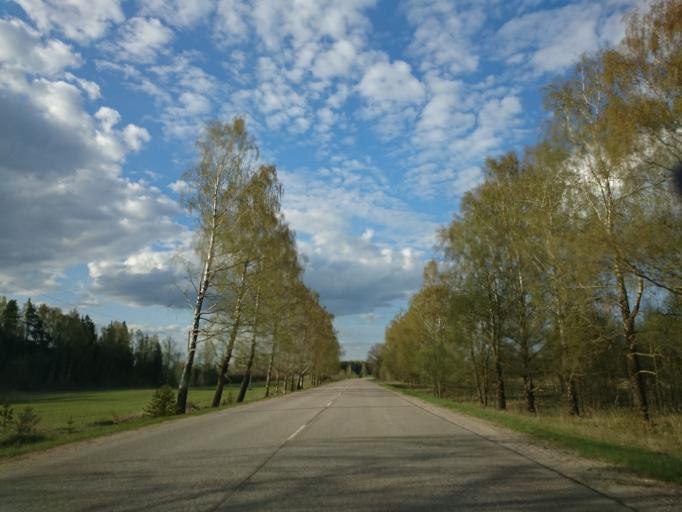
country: LV
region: Kuldigas Rajons
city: Kuldiga
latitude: 56.8966
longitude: 21.8883
